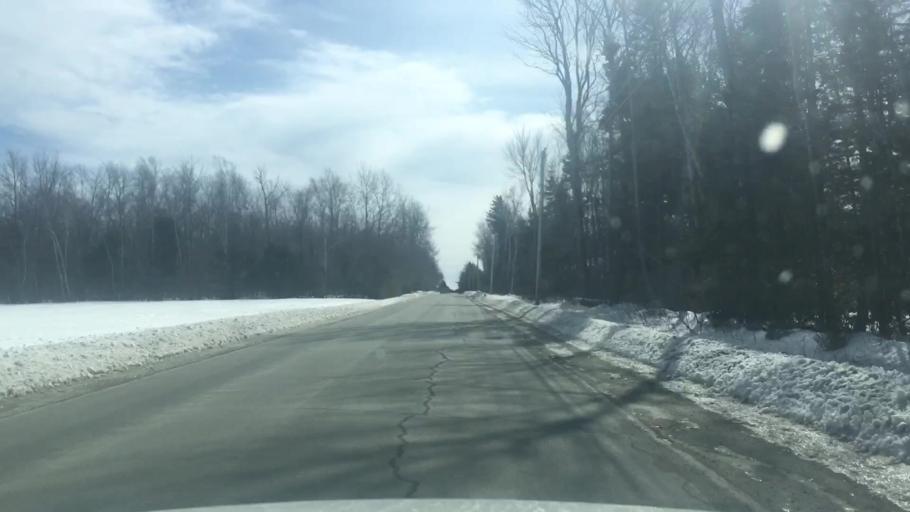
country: US
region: Maine
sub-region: Penobscot County
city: Holden
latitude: 44.7732
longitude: -68.6499
